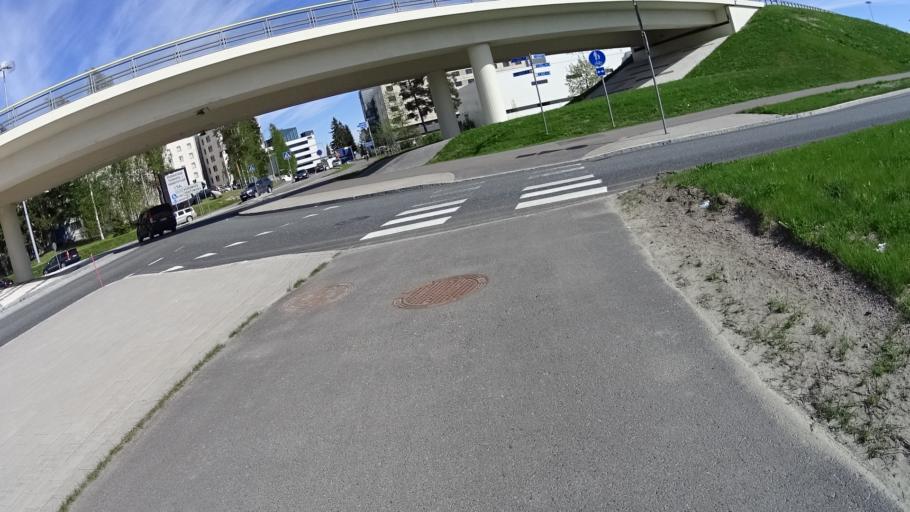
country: FI
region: Uusimaa
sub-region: Helsinki
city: Vantaa
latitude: 60.2969
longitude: 24.9585
